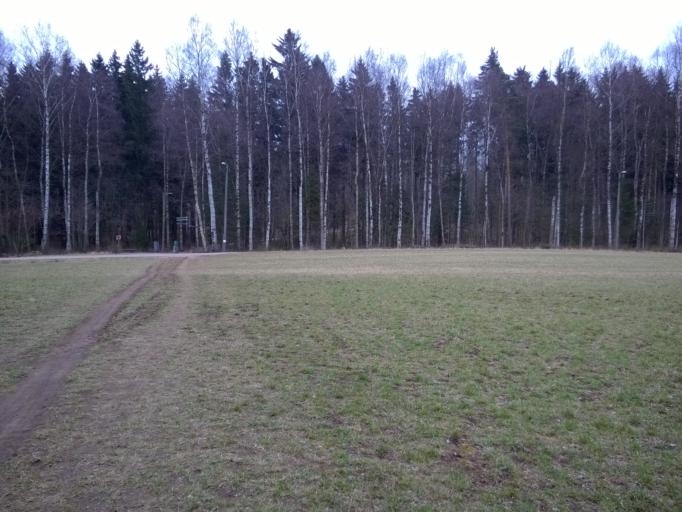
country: FI
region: Uusimaa
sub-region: Helsinki
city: Vantaa
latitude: 60.2166
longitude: 25.0320
